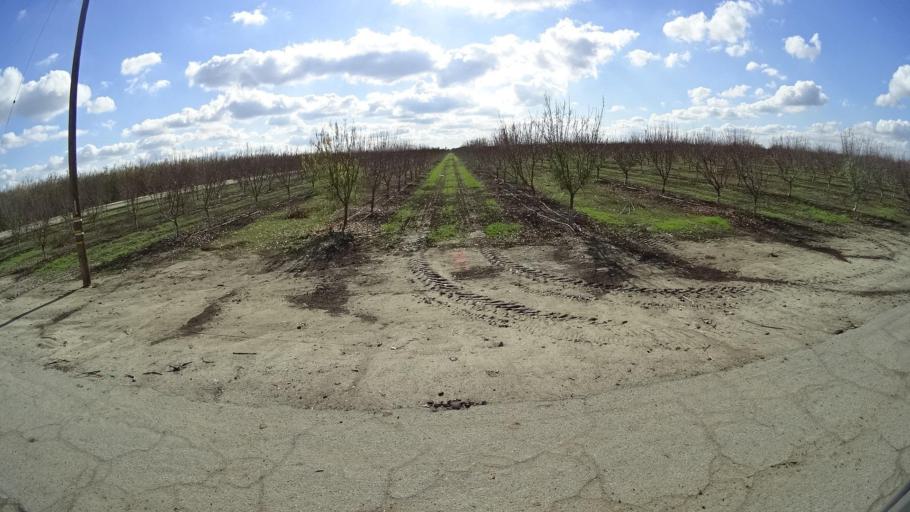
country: US
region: California
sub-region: Kern County
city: Wasco
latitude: 35.6669
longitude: -119.3125
